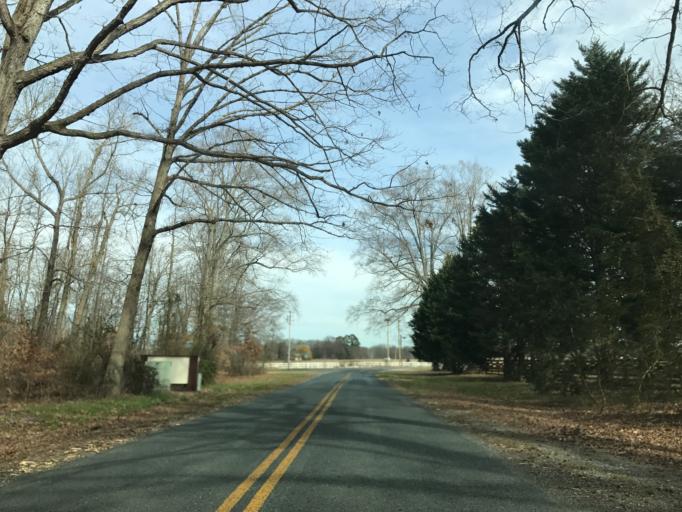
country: US
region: Maryland
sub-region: Queen Anne's County
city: Centreville
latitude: 39.0605
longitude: -76.1198
